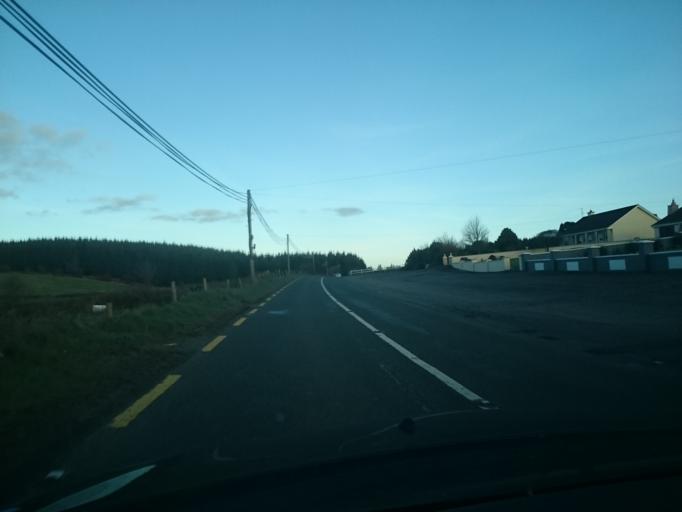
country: IE
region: Connaught
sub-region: Maigh Eo
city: Kiltamagh
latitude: 53.7954
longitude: -9.0971
